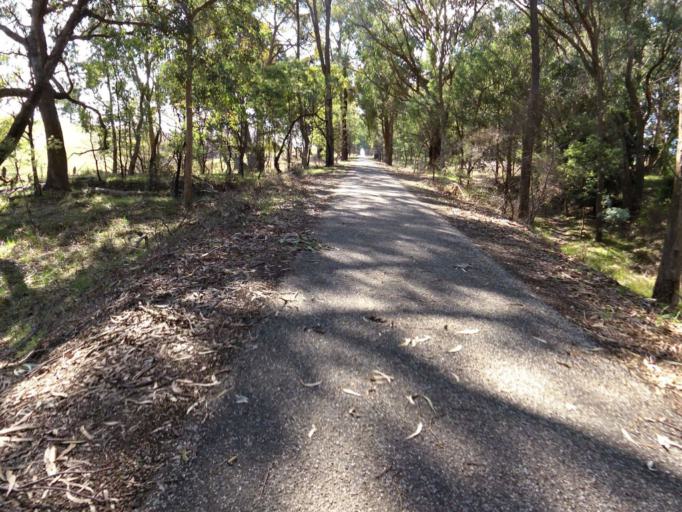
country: AU
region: Victoria
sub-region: Wangaratta
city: Wangaratta
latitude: -36.4018
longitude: 146.6431
